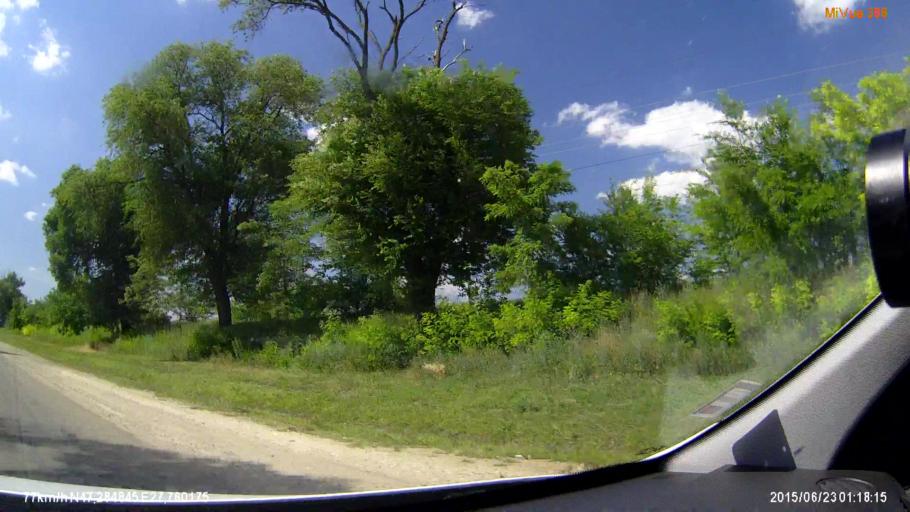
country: RO
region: Iasi
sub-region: Comuna Ungheni
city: Bosia
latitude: 47.2848
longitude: 27.7604
